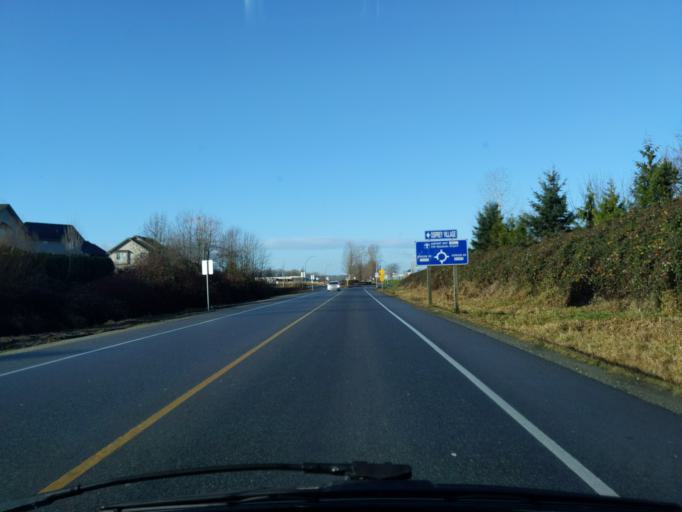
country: CA
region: British Columbia
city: Pitt Meadows
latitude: 49.2084
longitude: -122.6763
